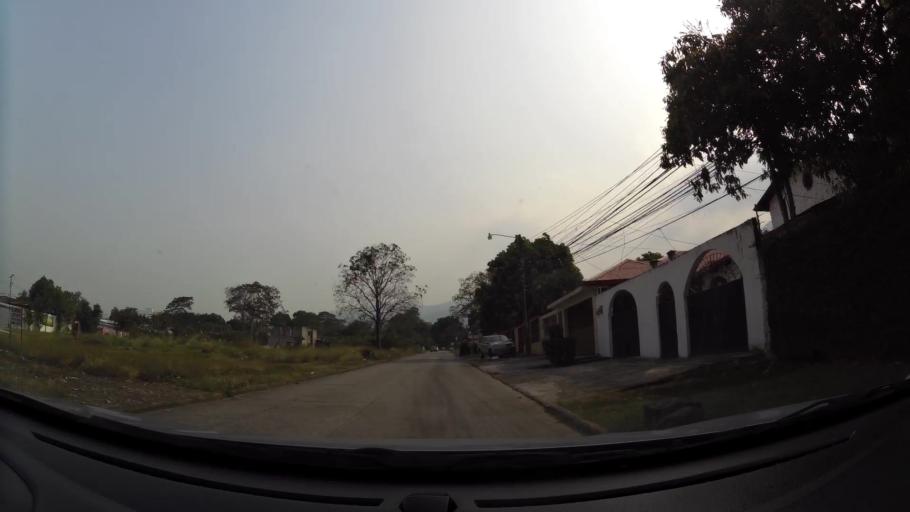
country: HN
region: Cortes
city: El Zapotal del Norte
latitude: 15.5159
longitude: -88.0385
